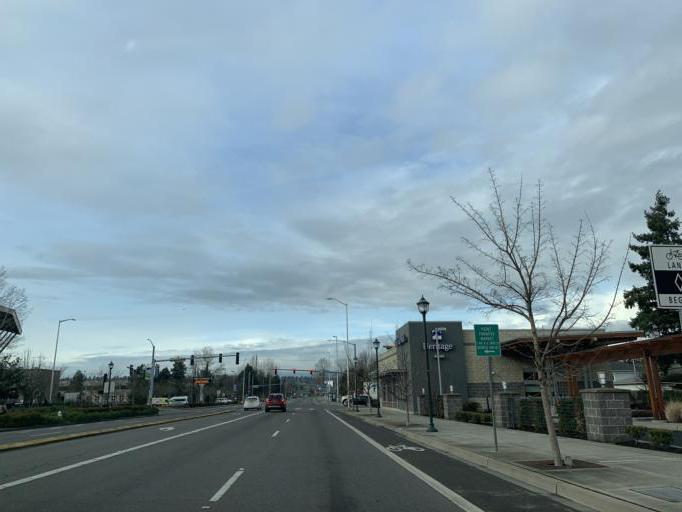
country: US
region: Washington
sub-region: King County
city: Kent
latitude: 47.3867
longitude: -122.2362
